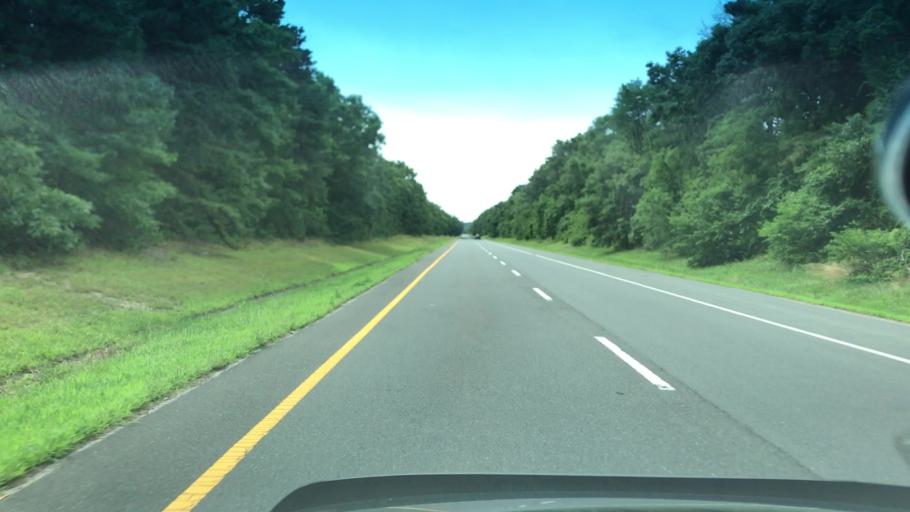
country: US
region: New York
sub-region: Suffolk County
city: East Shoreham
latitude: 40.9410
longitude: -72.8782
